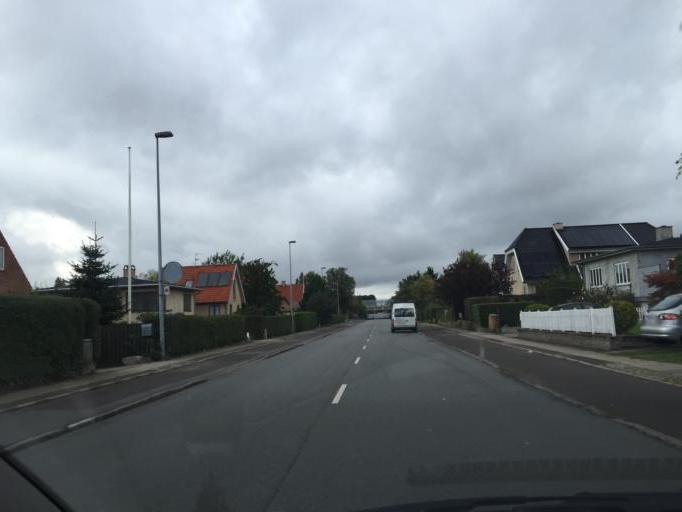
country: DK
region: Capital Region
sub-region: Gladsaxe Municipality
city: Buddinge
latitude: 55.7467
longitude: 12.4722
